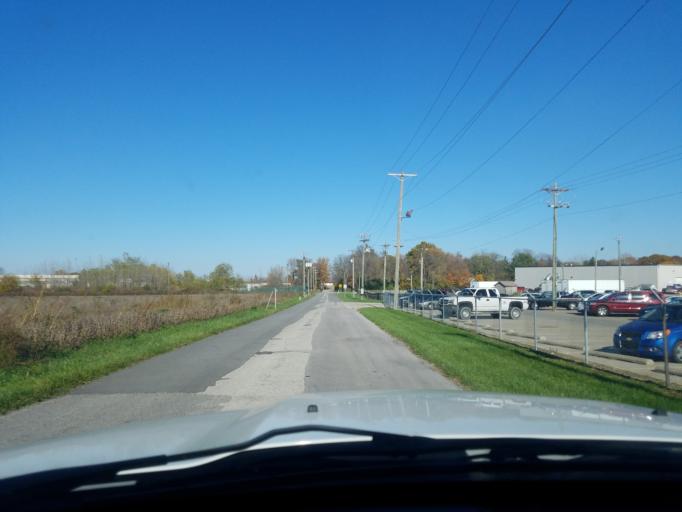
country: US
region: Indiana
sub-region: Montgomery County
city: Crawfordsville
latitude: 40.0723
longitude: -86.8998
